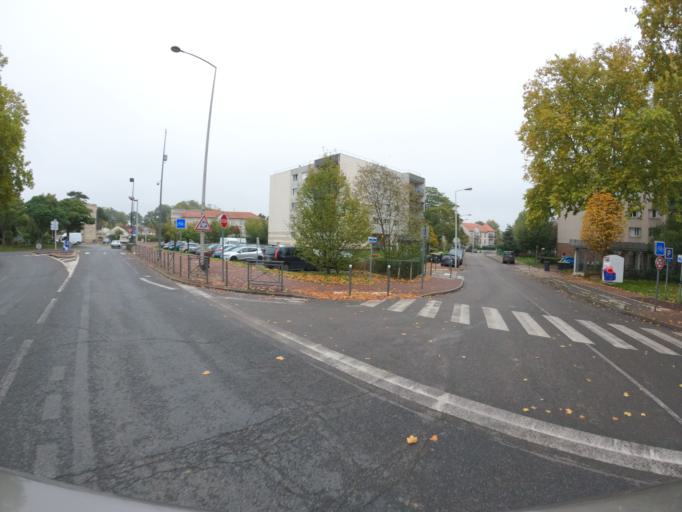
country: FR
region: Ile-de-France
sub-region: Departement du Val-de-Marne
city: Le Plessis-Trevise
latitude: 48.8071
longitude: 2.5576
